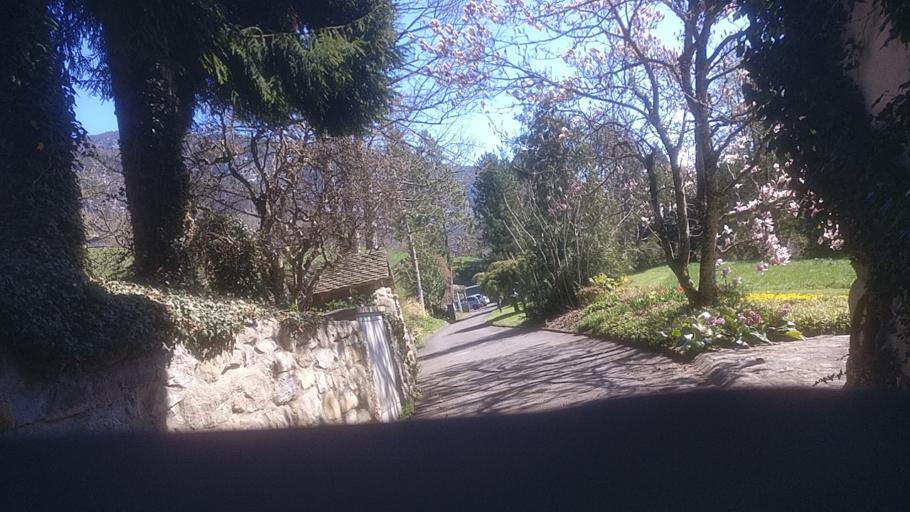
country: CH
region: Bern
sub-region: Thun District
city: Sigriswil
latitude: 46.7074
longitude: 7.7263
